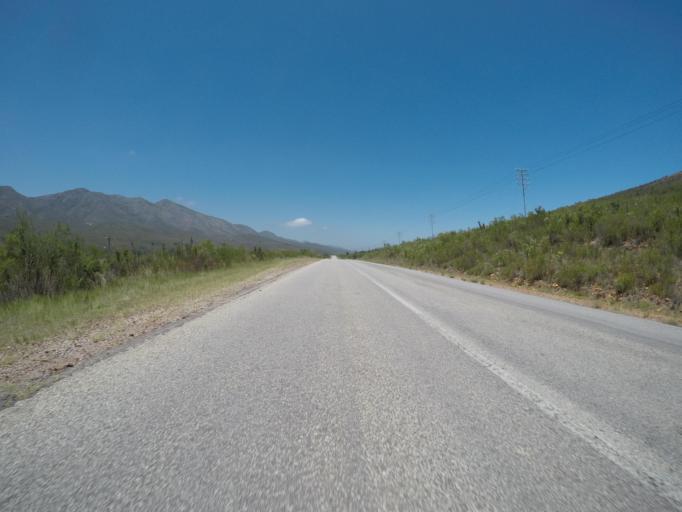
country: ZA
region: Eastern Cape
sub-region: Cacadu District Municipality
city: Kareedouw
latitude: -33.9066
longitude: 24.1503
